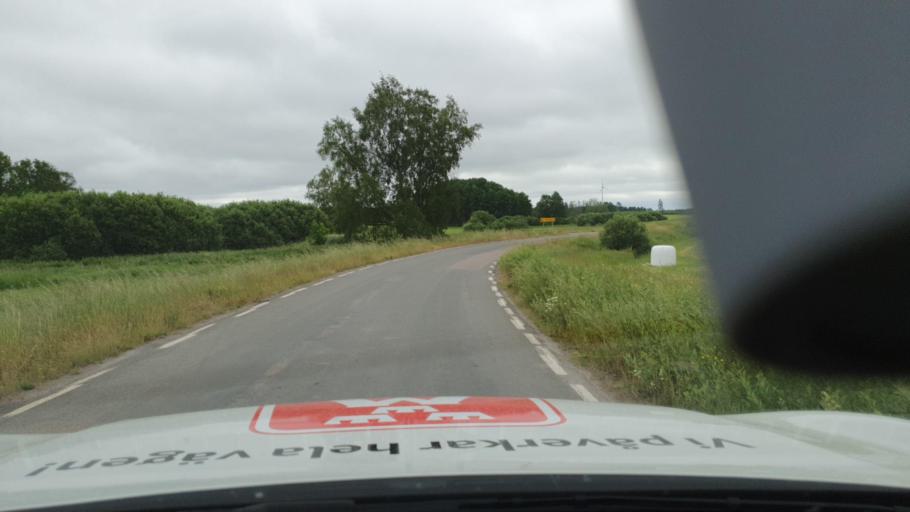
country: SE
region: Vaestra Goetaland
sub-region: Tibro Kommun
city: Tibro
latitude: 58.3877
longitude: 14.1206
